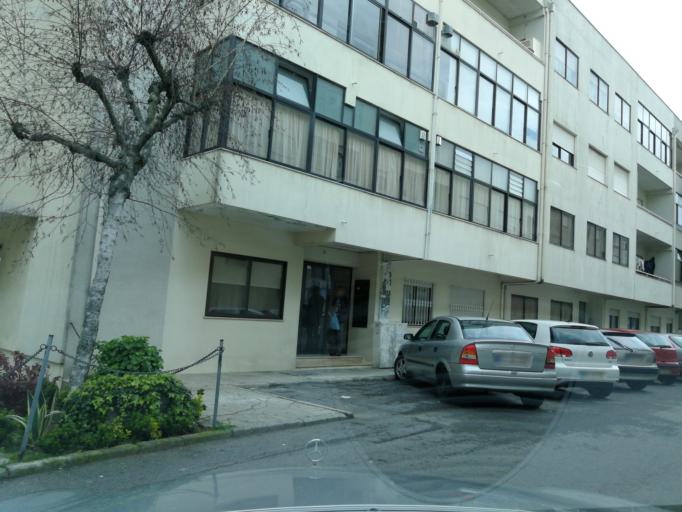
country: PT
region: Braga
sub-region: Braga
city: Braga
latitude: 41.5384
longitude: -8.4278
